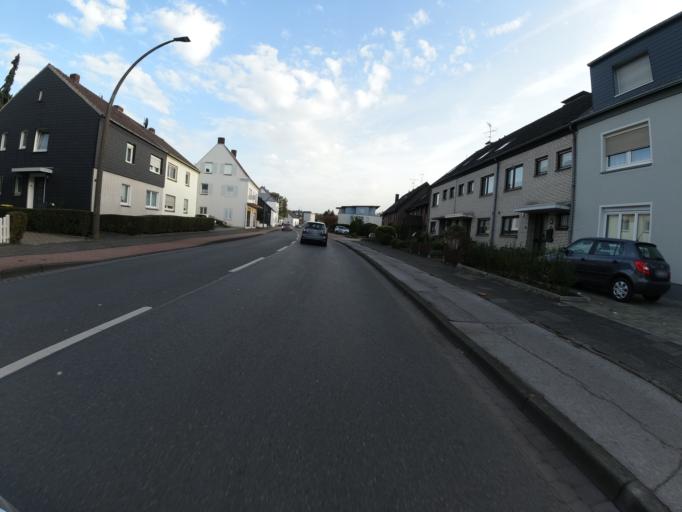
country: DE
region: North Rhine-Westphalia
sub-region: Regierungsbezirk Dusseldorf
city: Hochfeld
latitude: 51.4073
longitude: 6.6866
